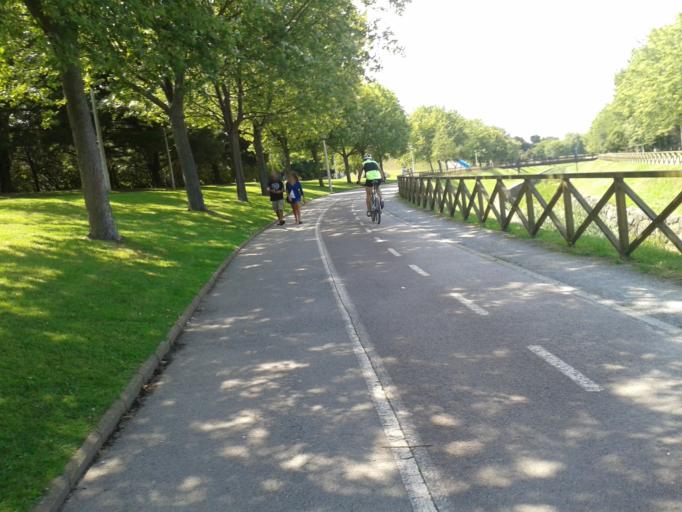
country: ES
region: Asturias
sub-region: Province of Asturias
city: Natahoyo
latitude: 43.5376
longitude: -5.6784
